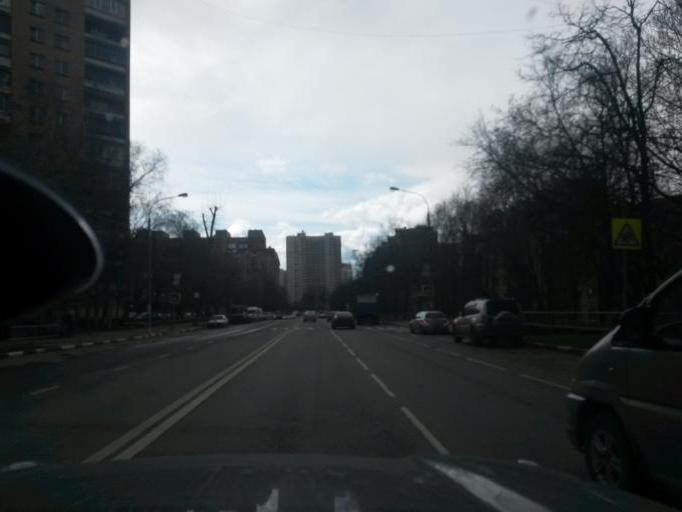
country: RU
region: Moskovskaya
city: Semenovskoye
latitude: 55.6785
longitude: 37.5440
